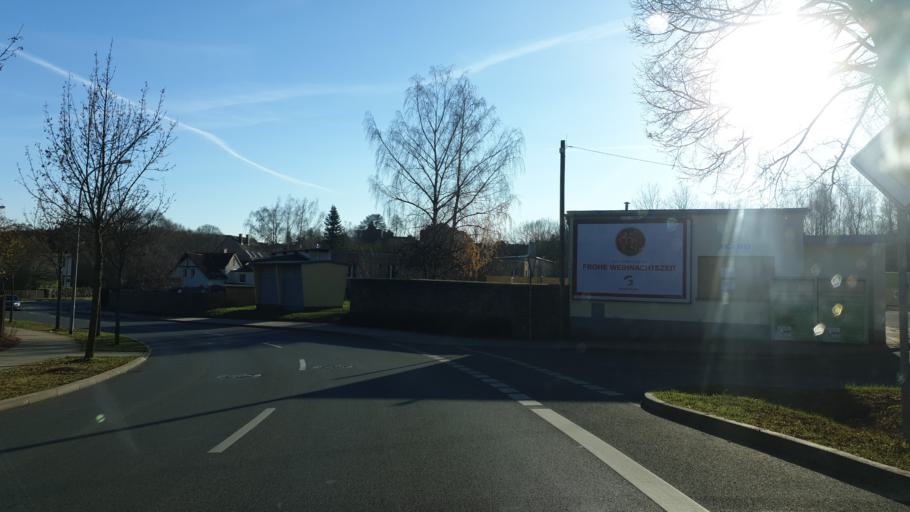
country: DE
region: Thuringia
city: Eisenberg
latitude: 50.9758
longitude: 11.8992
